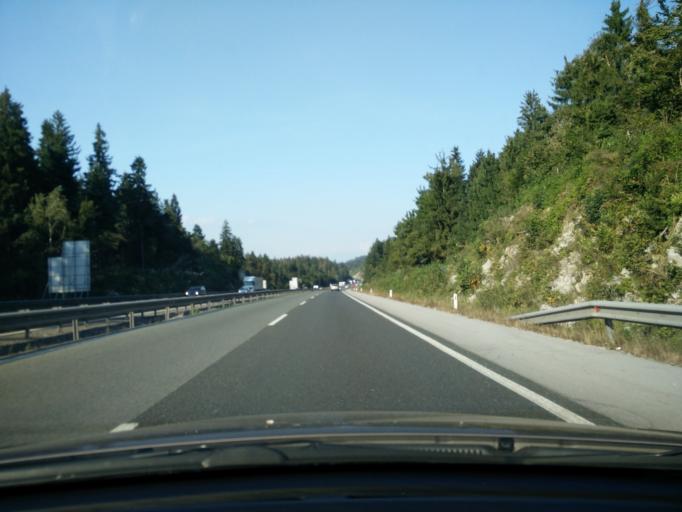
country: SI
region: Logatec
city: Logatec
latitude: 45.9118
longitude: 14.2600
